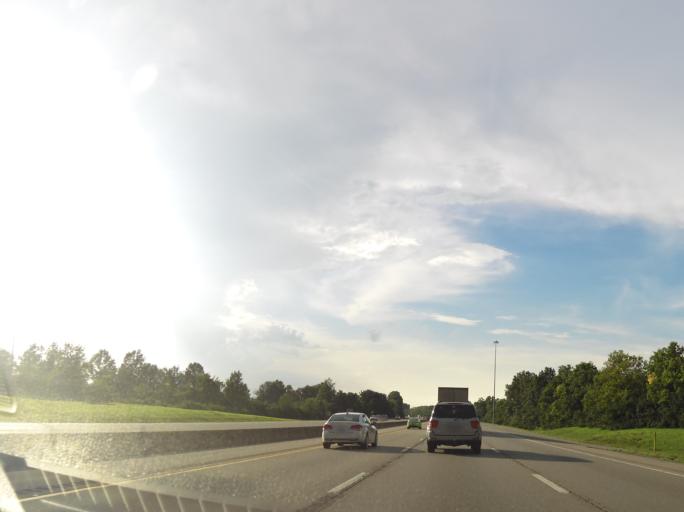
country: US
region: Kentucky
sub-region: Fayette County
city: Lexington-Fayette
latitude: 38.0799
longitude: -84.4587
